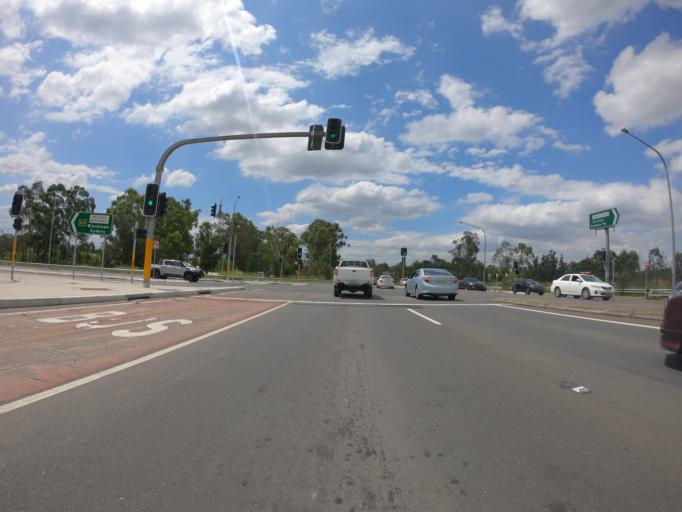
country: AU
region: New South Wales
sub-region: Blacktown
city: Mount Druitt
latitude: -33.7834
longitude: 150.7710
